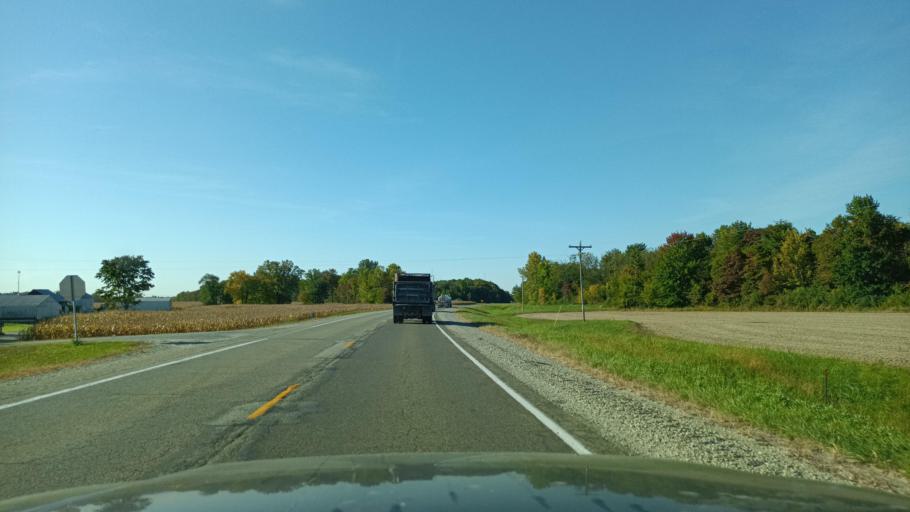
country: US
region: Illinois
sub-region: Clark County
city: Marshall
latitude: 39.4453
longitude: -87.6825
